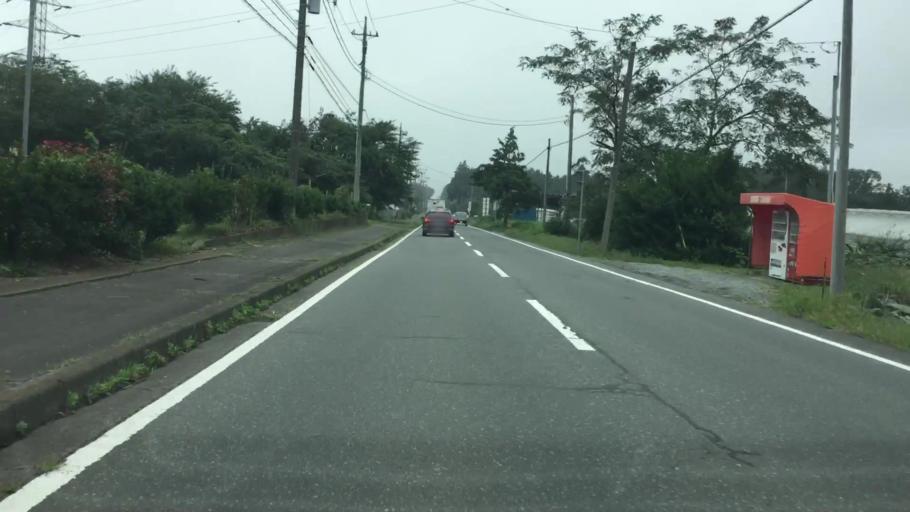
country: JP
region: Shizuoka
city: Fujinomiya
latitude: 35.3397
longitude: 138.5949
